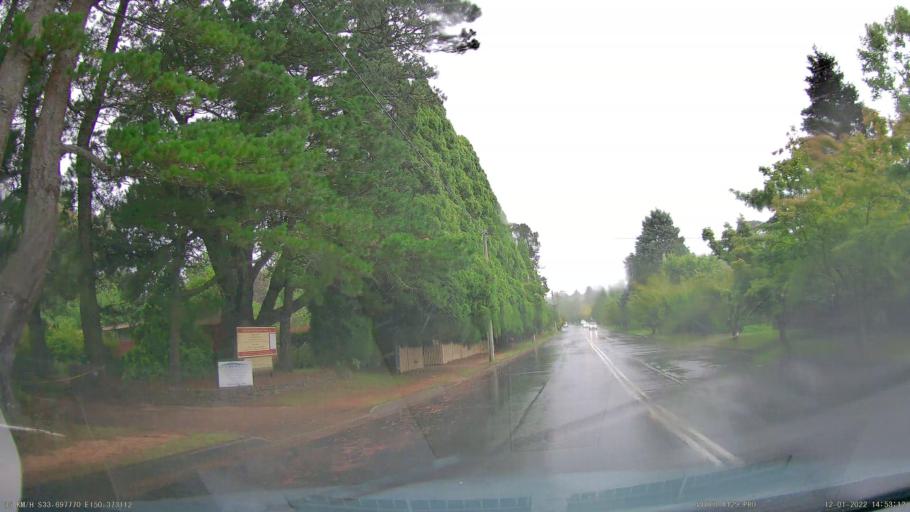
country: AU
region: New South Wales
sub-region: Blue Mountains Municipality
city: Leura
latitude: -33.6979
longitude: 150.3731
